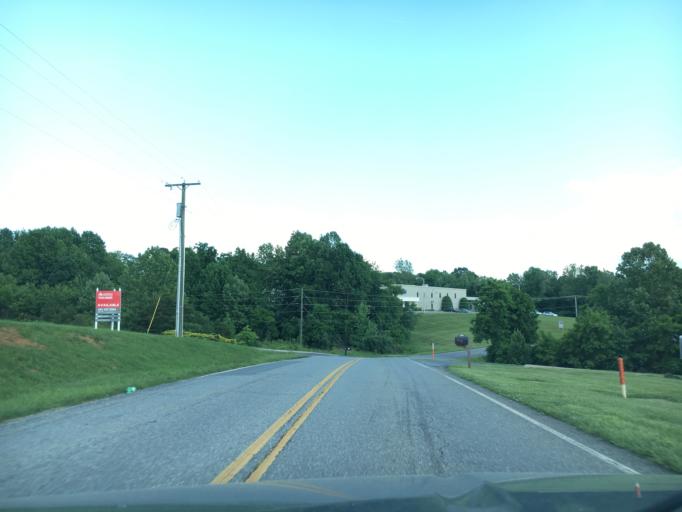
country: US
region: Virginia
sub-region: Bedford County
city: Forest
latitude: 37.3778
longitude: -79.2524
